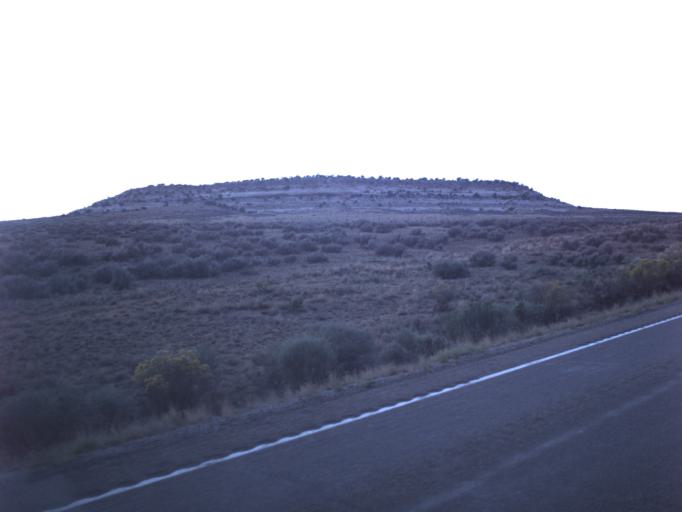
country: US
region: Utah
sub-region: San Juan County
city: Monticello
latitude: 38.0920
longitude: -109.3572
